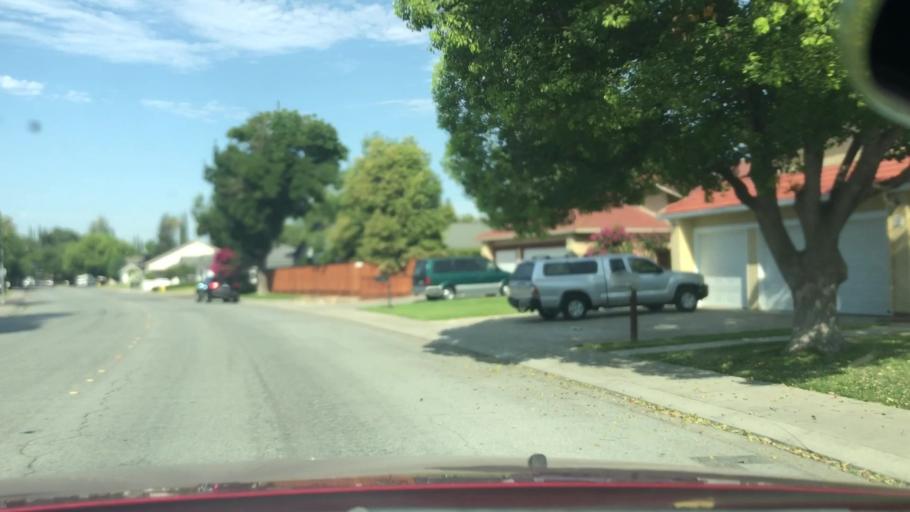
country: US
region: California
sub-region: San Joaquin County
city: Tracy
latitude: 37.7321
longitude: -121.4373
